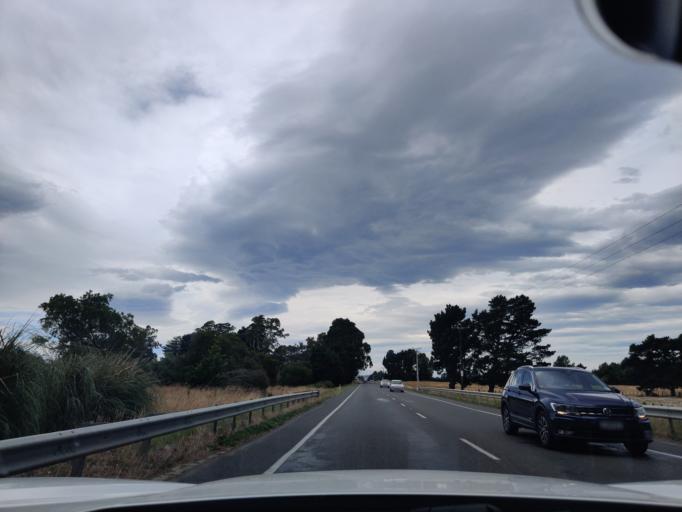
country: NZ
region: Wellington
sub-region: Masterton District
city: Masterton
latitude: -40.9851
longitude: 175.5790
